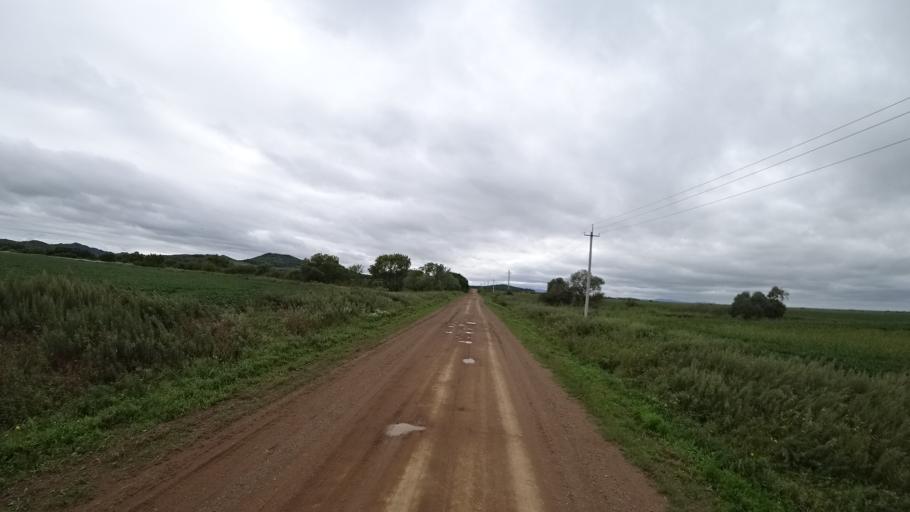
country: RU
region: Primorskiy
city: Chernigovka
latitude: 44.4887
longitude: 132.5727
